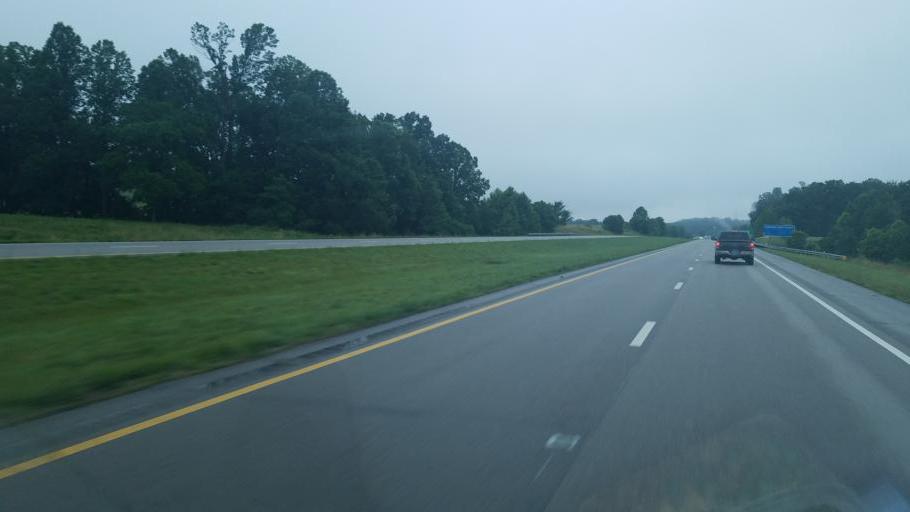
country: US
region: Ohio
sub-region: Jackson County
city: Oak Hill
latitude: 38.8852
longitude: -82.4107
